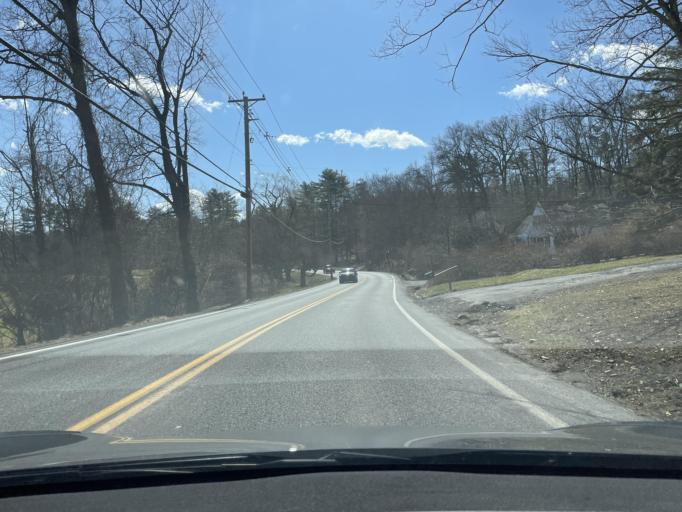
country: US
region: New York
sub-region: Ulster County
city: Woodstock
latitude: 42.0333
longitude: -74.1093
